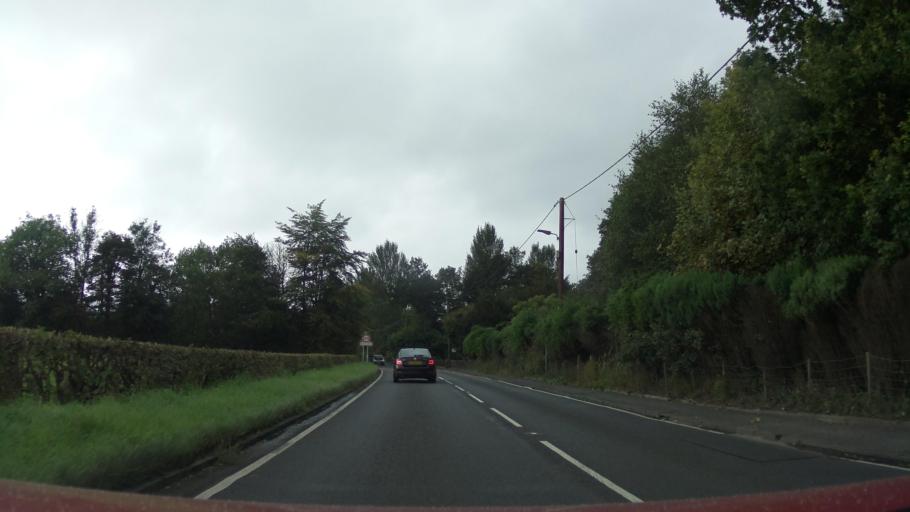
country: GB
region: Scotland
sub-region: Clackmannanshire
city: Menstrie
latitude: 56.1499
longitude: -3.8798
